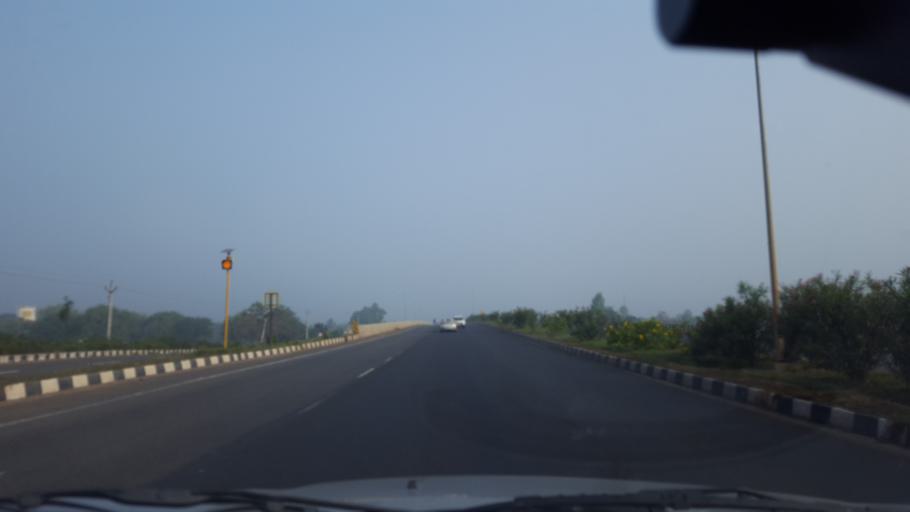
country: IN
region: Andhra Pradesh
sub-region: Prakasam
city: Ongole
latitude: 15.3879
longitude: 80.0393
